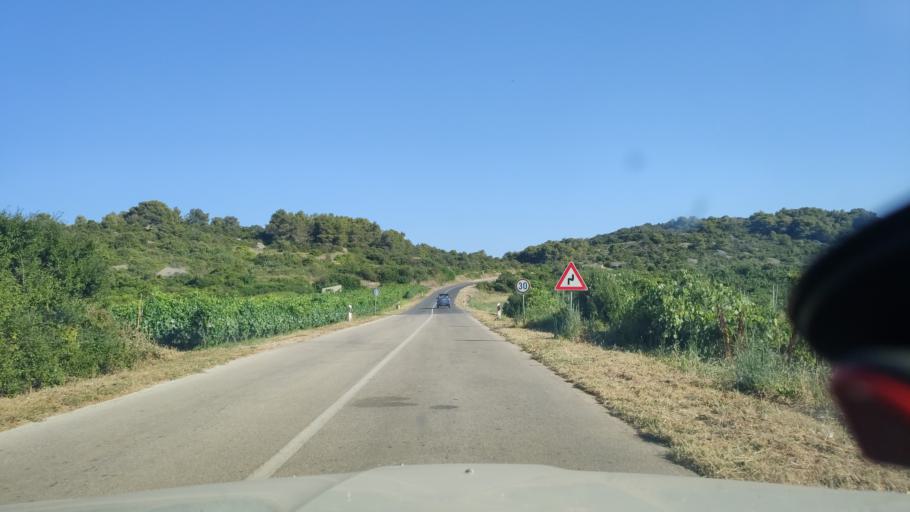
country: HR
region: Splitsko-Dalmatinska
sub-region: Grad Vis
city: Vis
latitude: 43.0406
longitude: 16.1998
